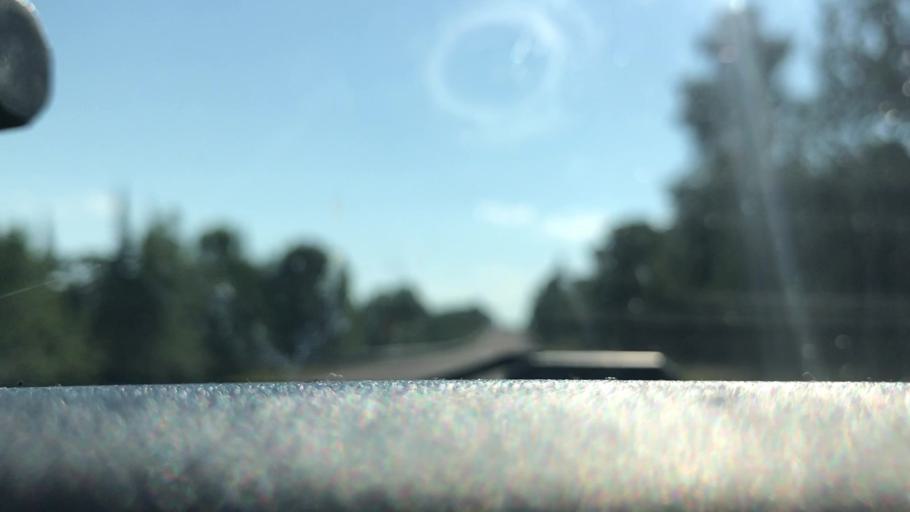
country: US
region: Minnesota
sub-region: Cook County
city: Grand Marais
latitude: 47.8307
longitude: -89.9834
